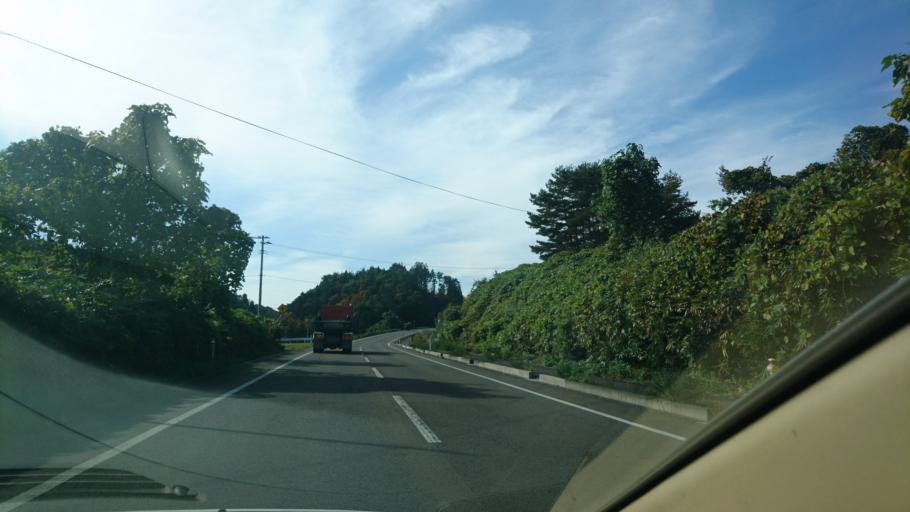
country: JP
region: Iwate
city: Mizusawa
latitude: 39.1495
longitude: 141.2209
